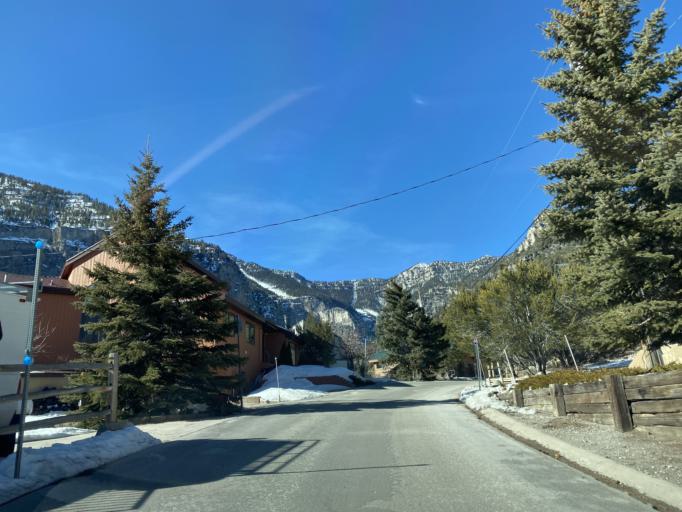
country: US
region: Nevada
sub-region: Nye County
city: Pahrump
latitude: 36.2652
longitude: -115.6569
